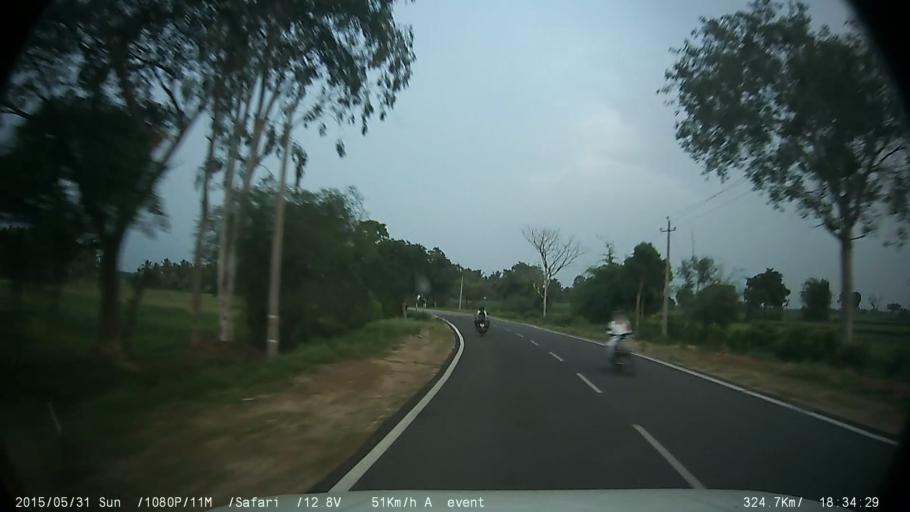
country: IN
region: Karnataka
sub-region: Mysore
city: Nanjangud
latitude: 12.1440
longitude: 76.7561
